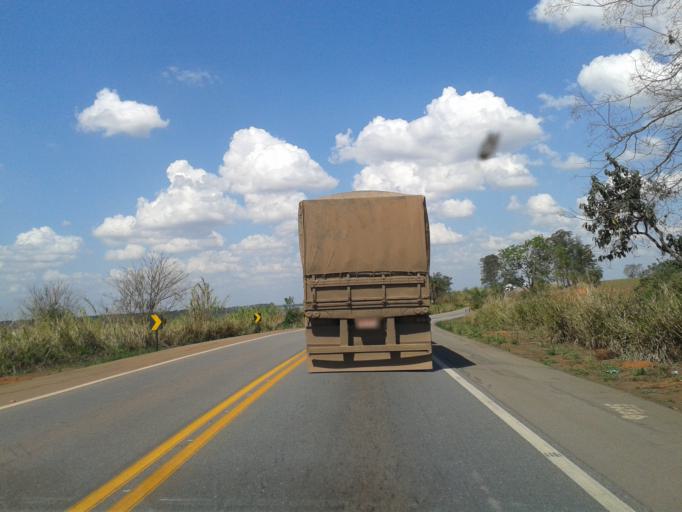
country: BR
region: Minas Gerais
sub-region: Luz
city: Luz
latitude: -19.7578
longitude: -45.8091
